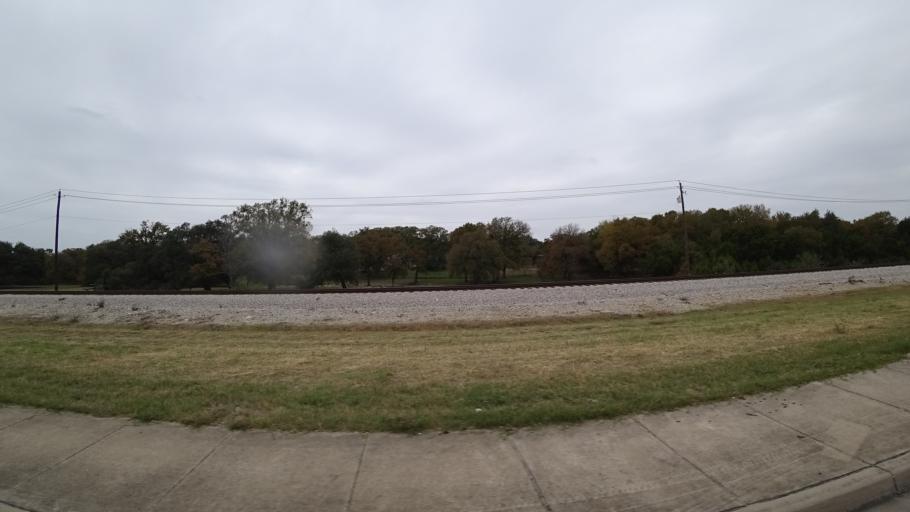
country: US
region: Texas
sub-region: Travis County
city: Wells Branch
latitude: 30.4307
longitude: -97.7014
